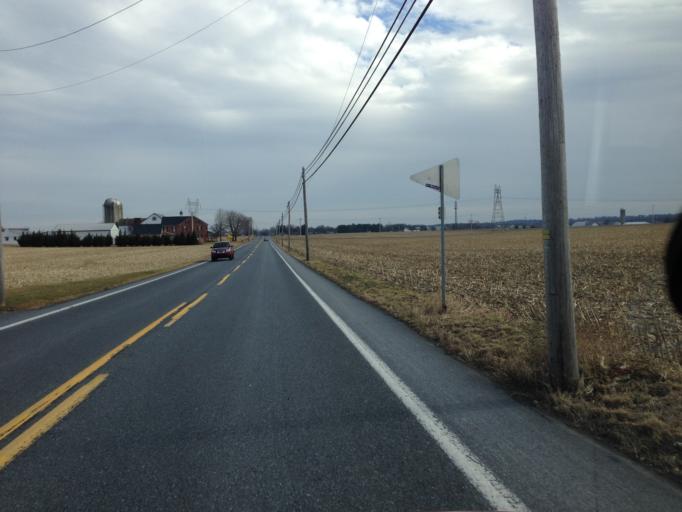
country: US
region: Pennsylvania
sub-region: Lancaster County
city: Lititz
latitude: 40.1725
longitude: -76.3342
